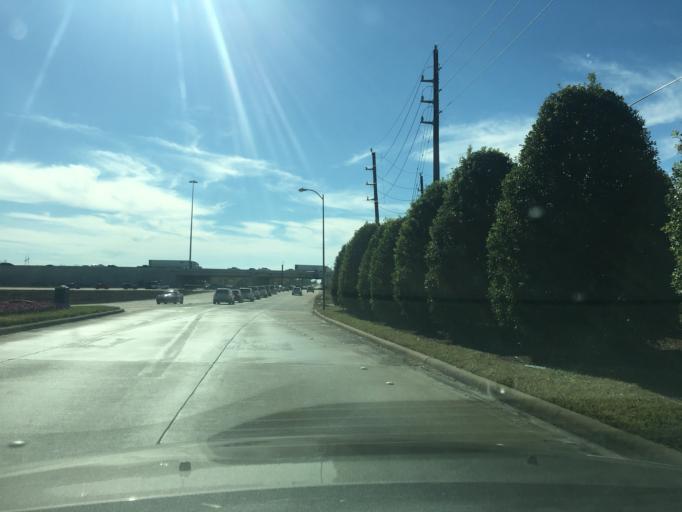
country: US
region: Texas
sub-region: Fort Bend County
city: Greatwood
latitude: 29.5585
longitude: -95.7158
